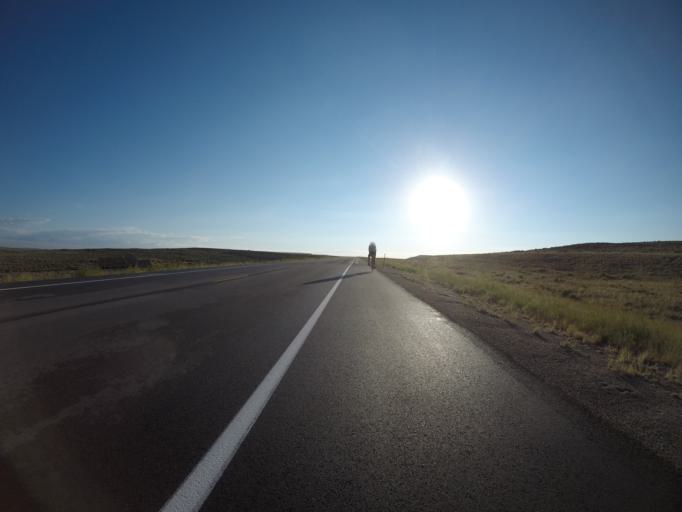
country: US
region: Wyoming
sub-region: Lincoln County
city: Kemmerer
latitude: 41.8764
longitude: -110.4434
